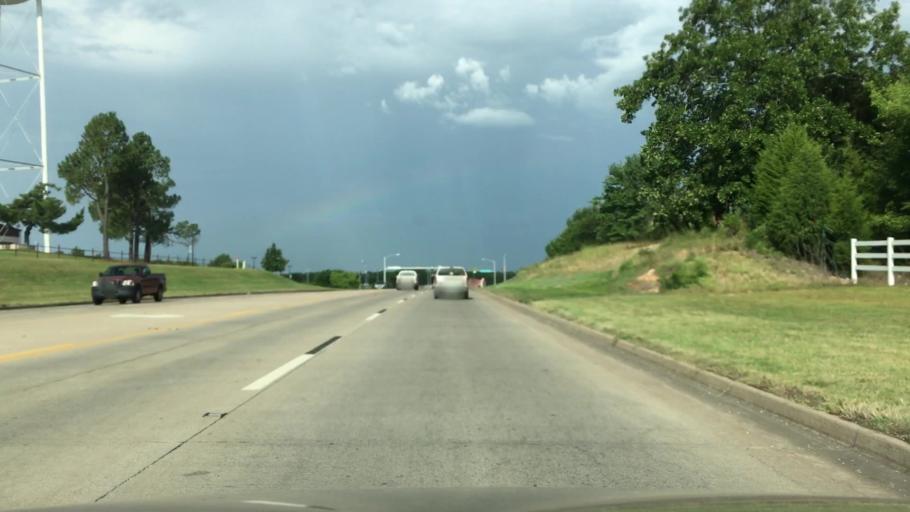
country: US
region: Oklahoma
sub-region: Cherokee County
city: Park Hill
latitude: 35.8502
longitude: -95.0005
